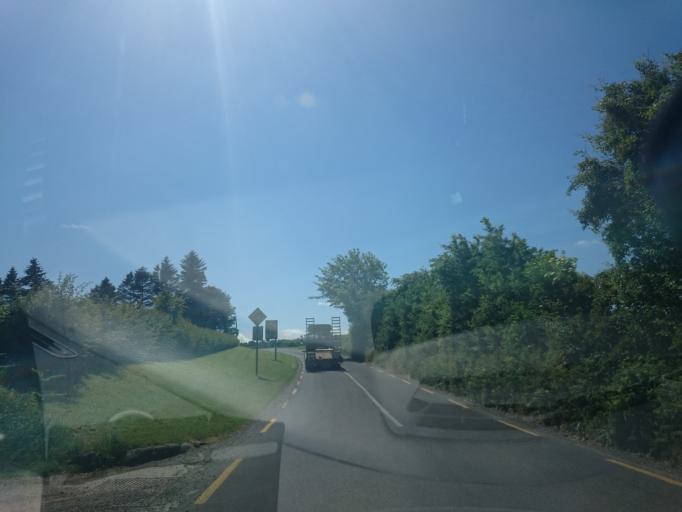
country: IE
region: Leinster
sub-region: Kilkenny
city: Graiguenamanagh
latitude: 52.6005
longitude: -6.9929
